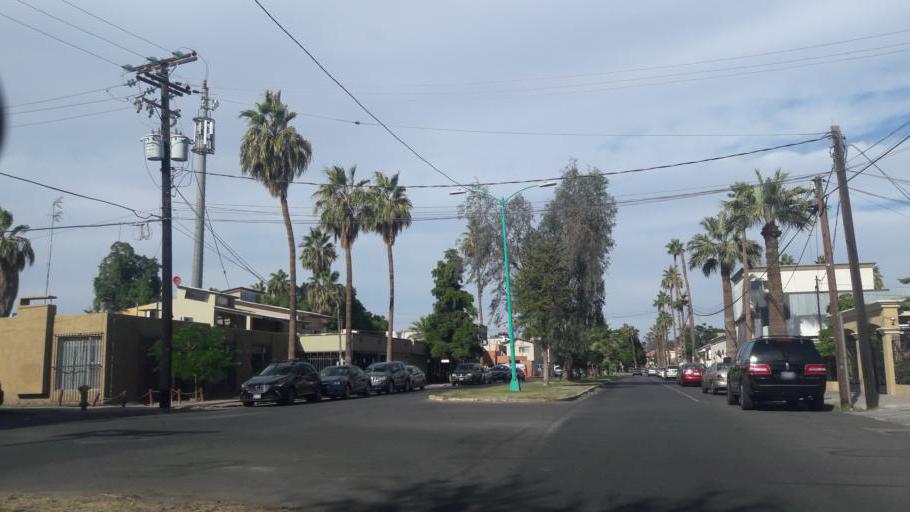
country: MX
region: Baja California
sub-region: Mexicali
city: Mexicali
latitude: 32.6513
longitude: -115.4505
